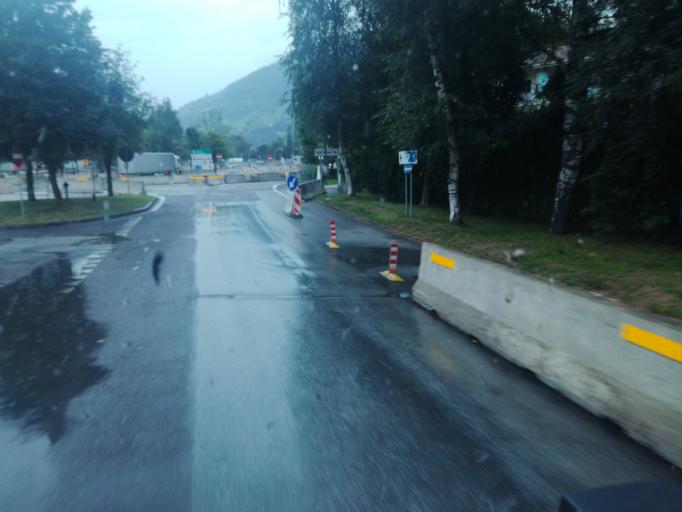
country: IT
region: Trentino-Alto Adige
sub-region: Bolzano
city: Vipiteno
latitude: 46.8809
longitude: 11.4362
